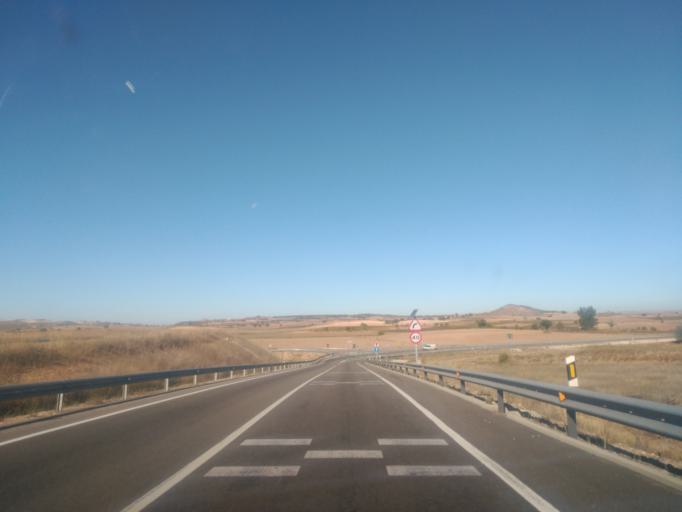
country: ES
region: Castille and Leon
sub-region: Provincia de Burgos
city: Castrillo de la Vega
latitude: 41.6366
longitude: -3.7797
